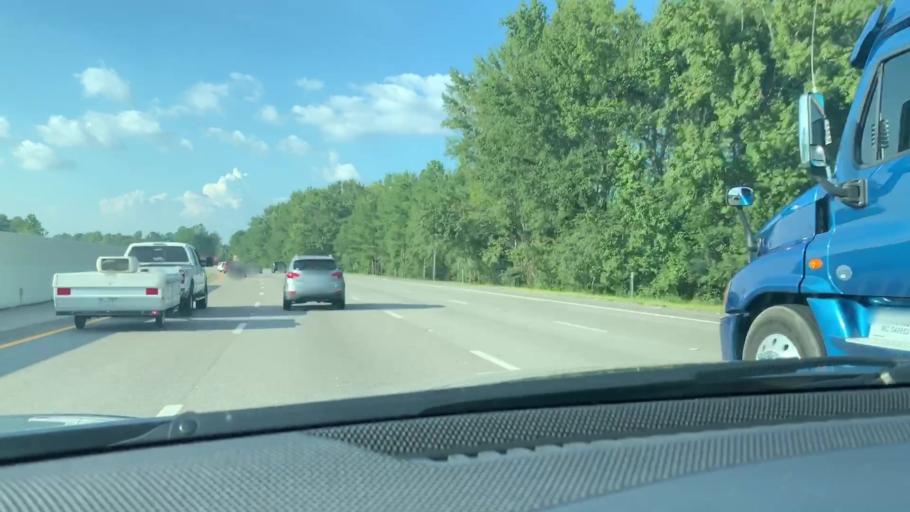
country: US
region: South Carolina
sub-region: Lexington County
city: Pineridge
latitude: 33.8841
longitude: -81.0372
